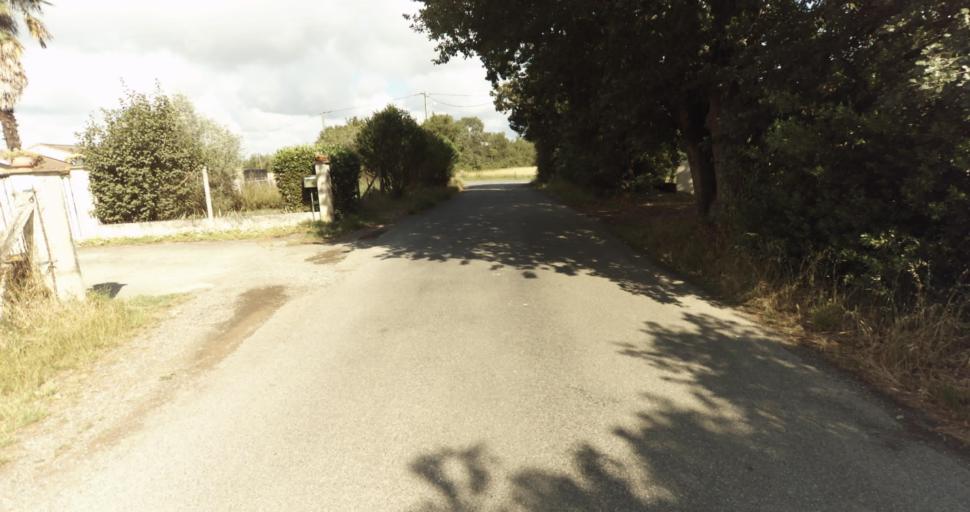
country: FR
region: Midi-Pyrenees
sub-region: Departement de la Haute-Garonne
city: Fontenilles
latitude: 43.5641
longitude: 1.2143
